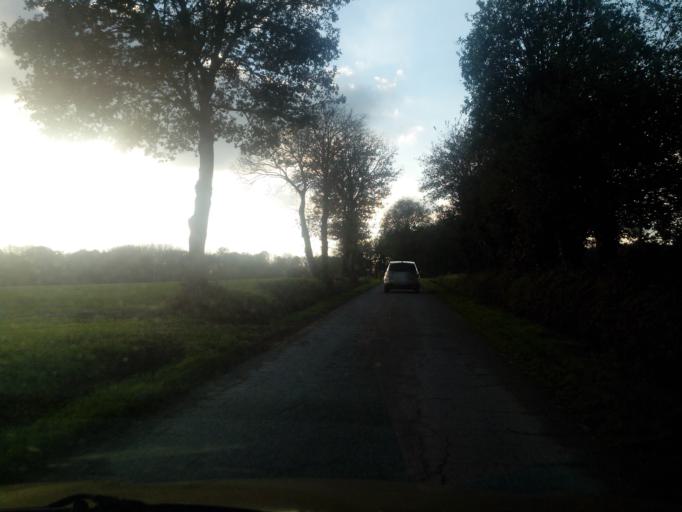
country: FR
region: Brittany
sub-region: Departement du Morbihan
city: Meneac
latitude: 48.1206
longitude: -2.3967
